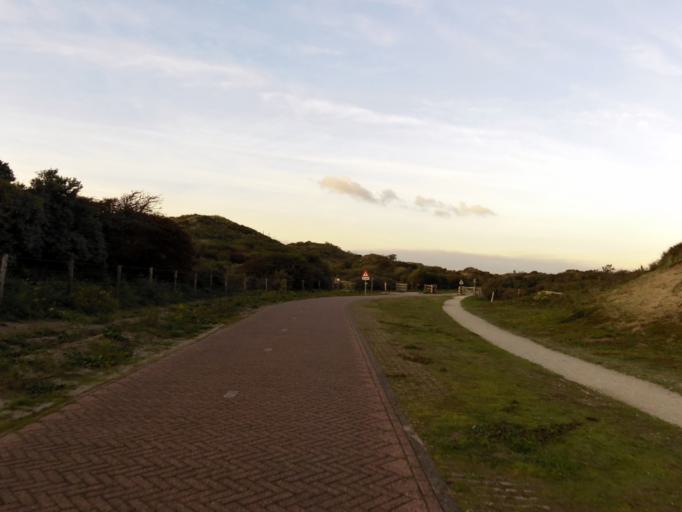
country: NL
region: South Holland
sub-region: Gemeente Den Haag
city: Scheveningen
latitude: 52.1291
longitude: 4.3107
